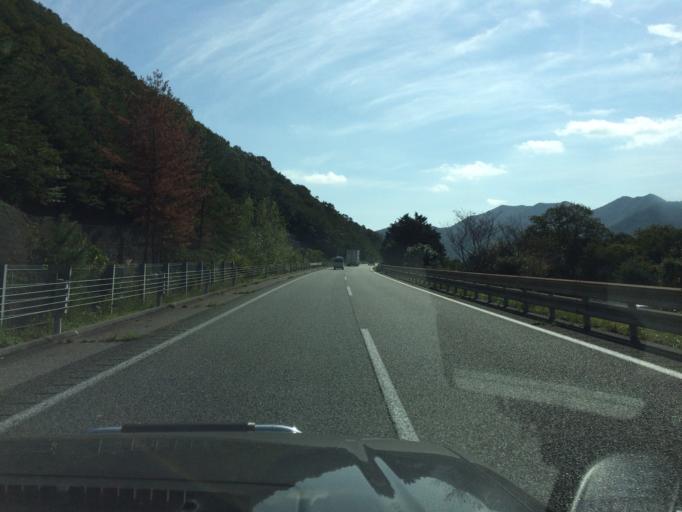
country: JP
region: Hyogo
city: Sasayama
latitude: 35.0118
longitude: 135.1622
